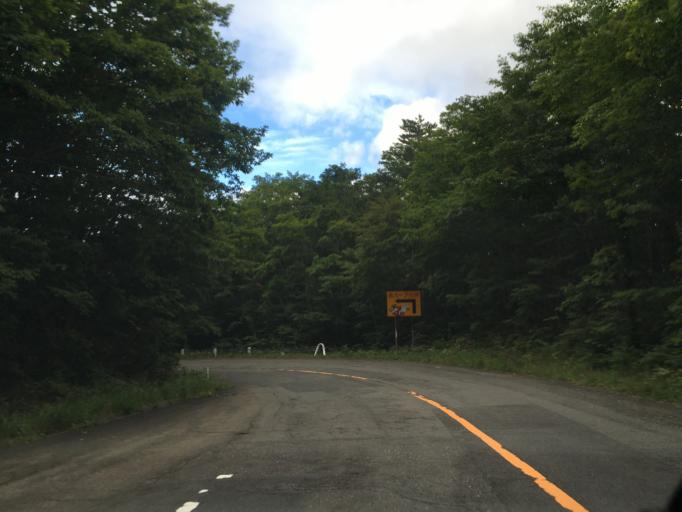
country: JP
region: Fukushima
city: Inawashiro
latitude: 37.5740
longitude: 140.2506
